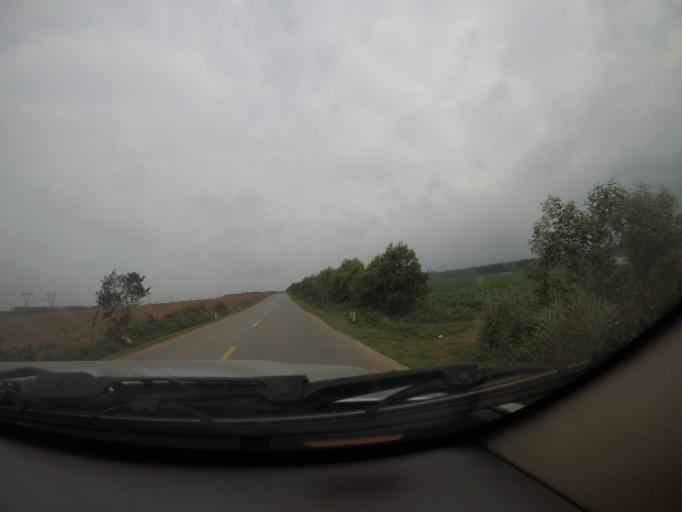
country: VN
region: Quang Binh
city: Hoan Lao
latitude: 17.5159
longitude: 106.4903
